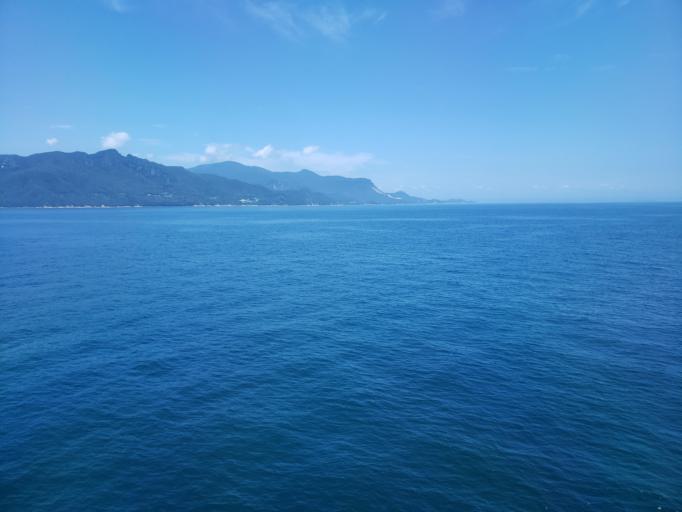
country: JP
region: Kagawa
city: Tonosho
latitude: 34.4317
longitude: 134.3680
